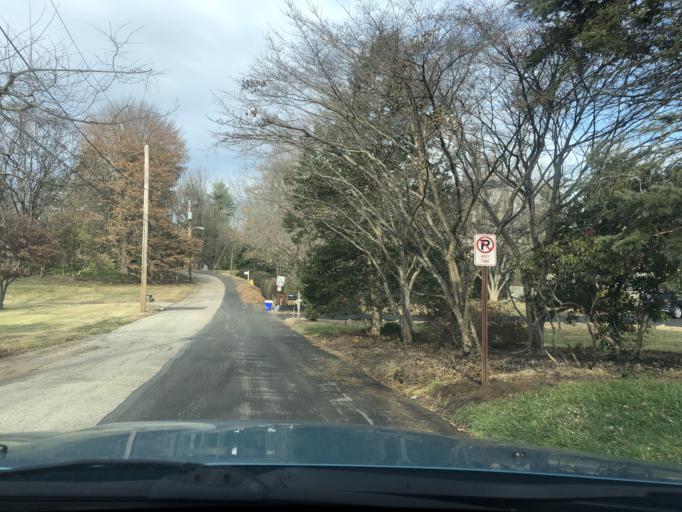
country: US
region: Pennsylvania
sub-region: Delaware County
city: Radnor
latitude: 40.0395
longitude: -75.3472
